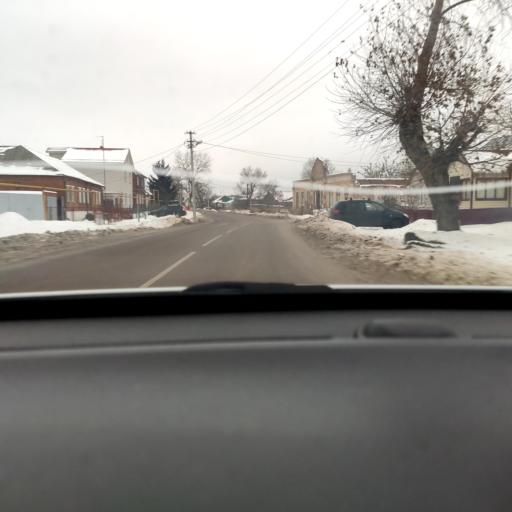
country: RU
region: Voronezj
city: Somovo
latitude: 51.7471
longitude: 39.3386
